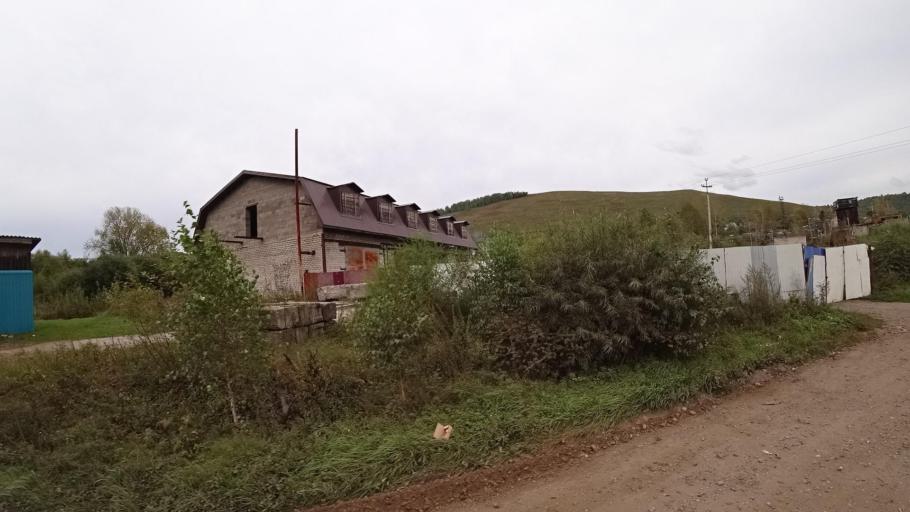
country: RU
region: Jewish Autonomous Oblast
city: Khingansk
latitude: 49.0249
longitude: 131.0540
